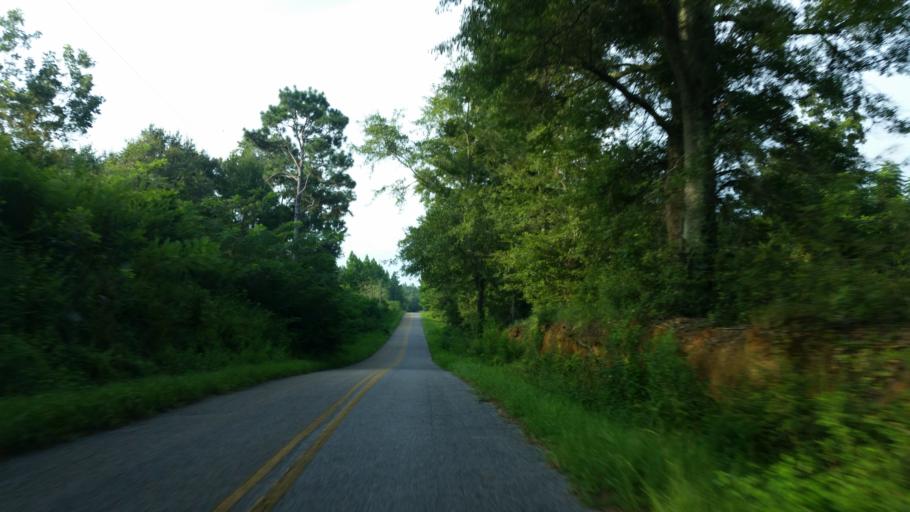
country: US
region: Alabama
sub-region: Escambia County
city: Atmore
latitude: 30.9800
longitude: -87.5712
